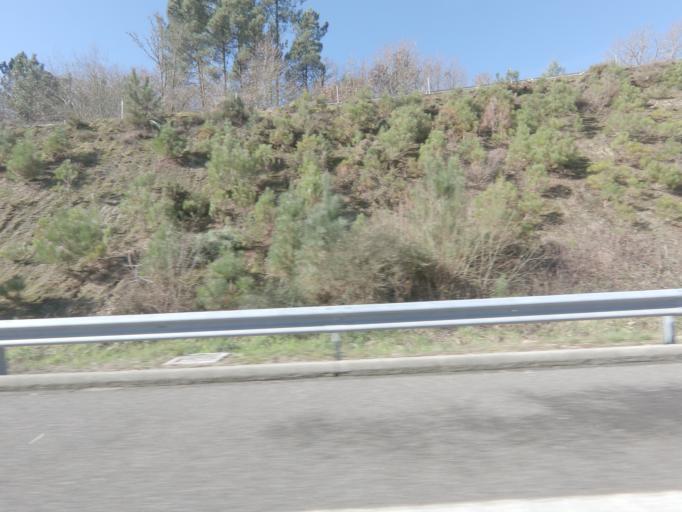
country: ES
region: Galicia
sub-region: Provincia de Ourense
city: Maside
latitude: 42.4411
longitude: -8.0180
